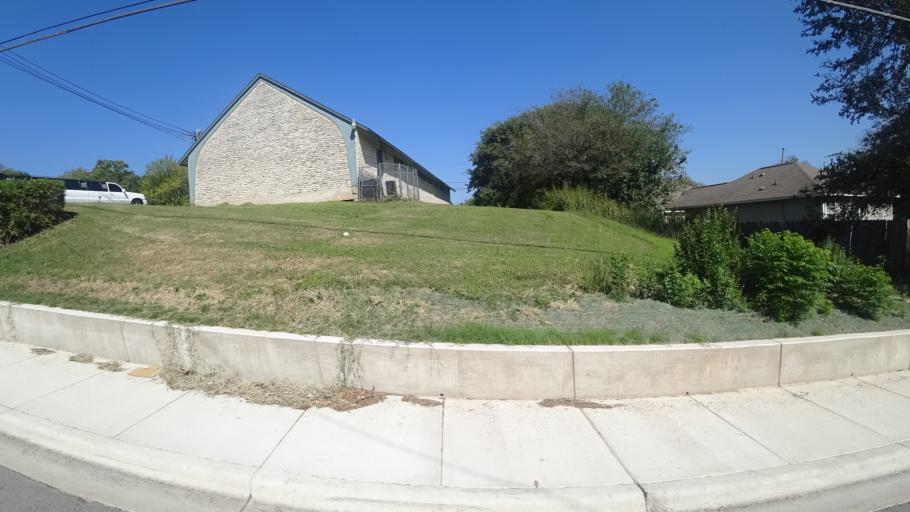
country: US
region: Texas
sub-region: Travis County
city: Austin
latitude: 30.3080
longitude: -97.6732
